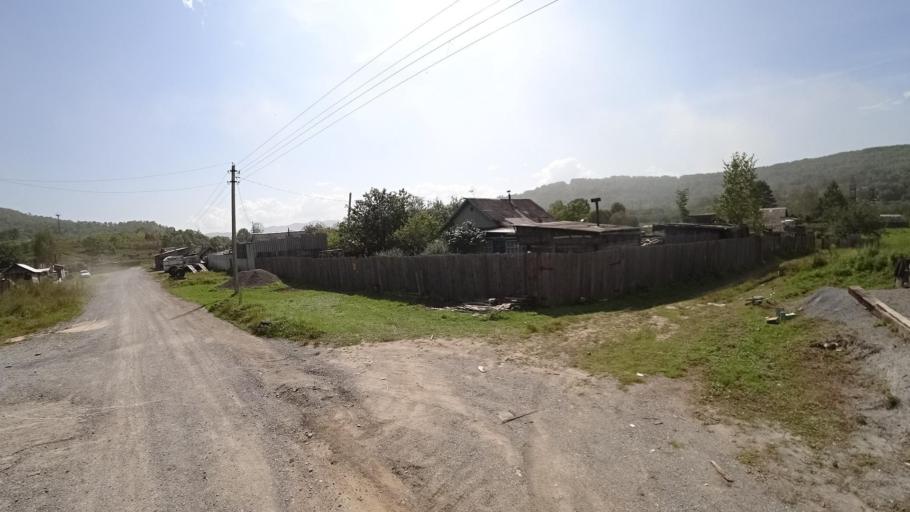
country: RU
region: Jewish Autonomous Oblast
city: Londoko
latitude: 49.0274
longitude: 131.9312
